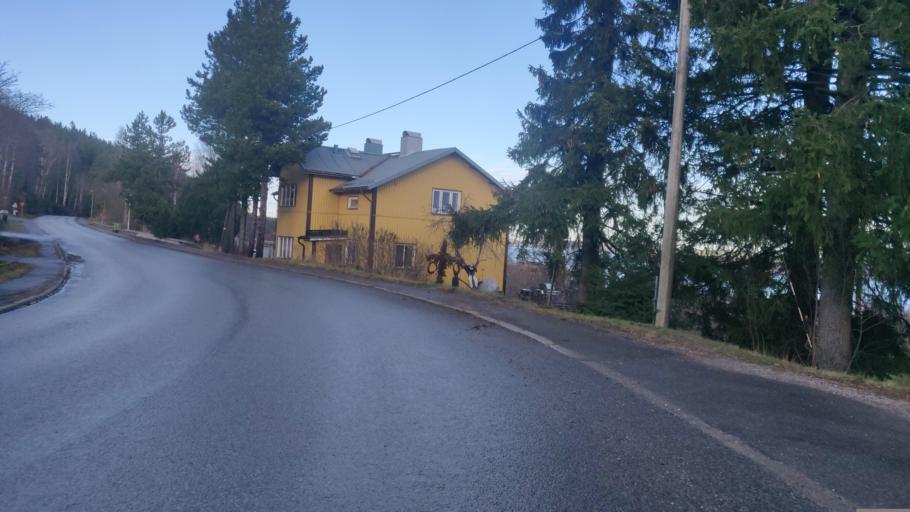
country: SE
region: Vaesternorrland
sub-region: Sundsvalls Kommun
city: Kvissleby
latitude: 62.3111
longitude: 17.3692
